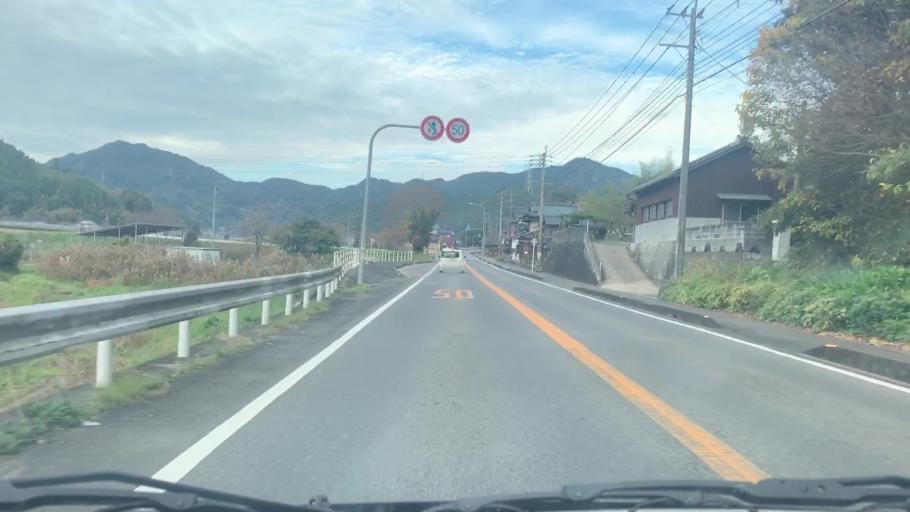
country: JP
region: Saga Prefecture
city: Ureshinomachi-shimojuku
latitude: 33.1299
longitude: 130.0330
